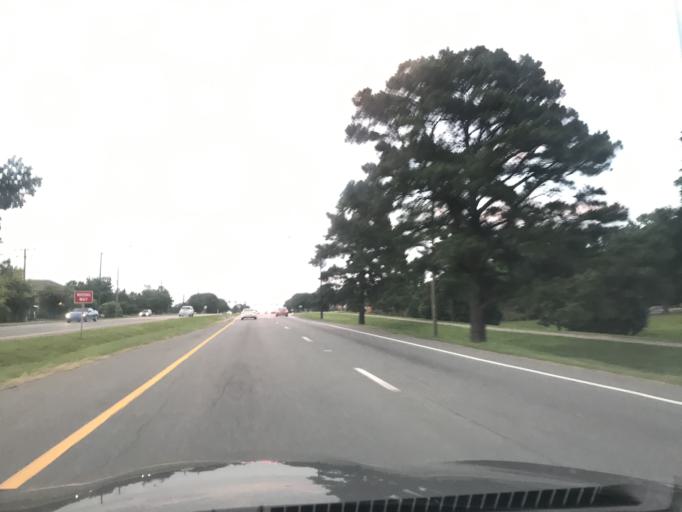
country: US
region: North Carolina
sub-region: Orange County
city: Chapel Hill
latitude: 35.9433
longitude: -79.0157
